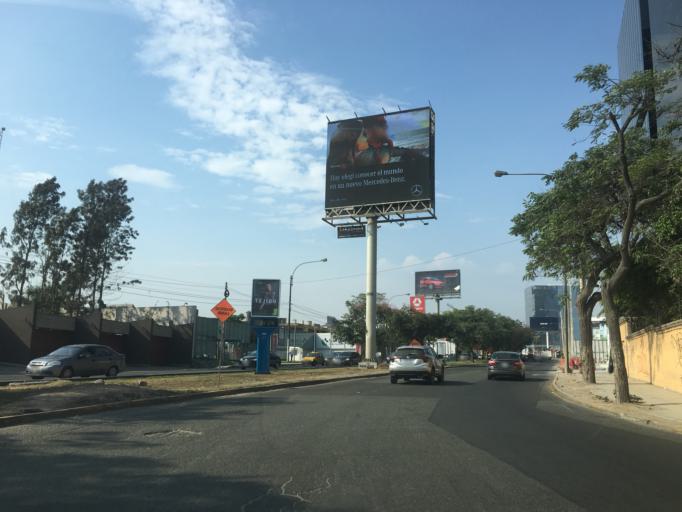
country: PE
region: Lima
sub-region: Lima
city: La Molina
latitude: -12.0830
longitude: -76.9694
